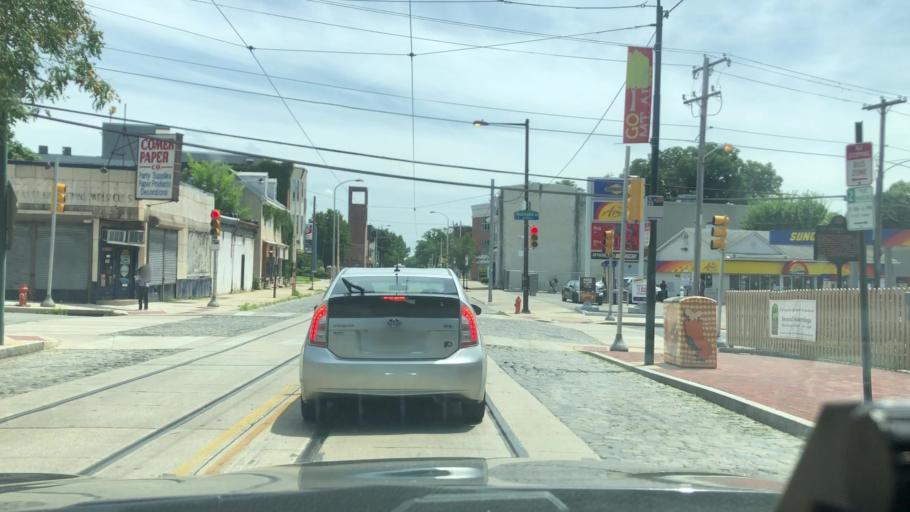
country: US
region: Pennsylvania
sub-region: Montgomery County
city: Wyndmoor
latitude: 40.0435
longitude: -75.1811
